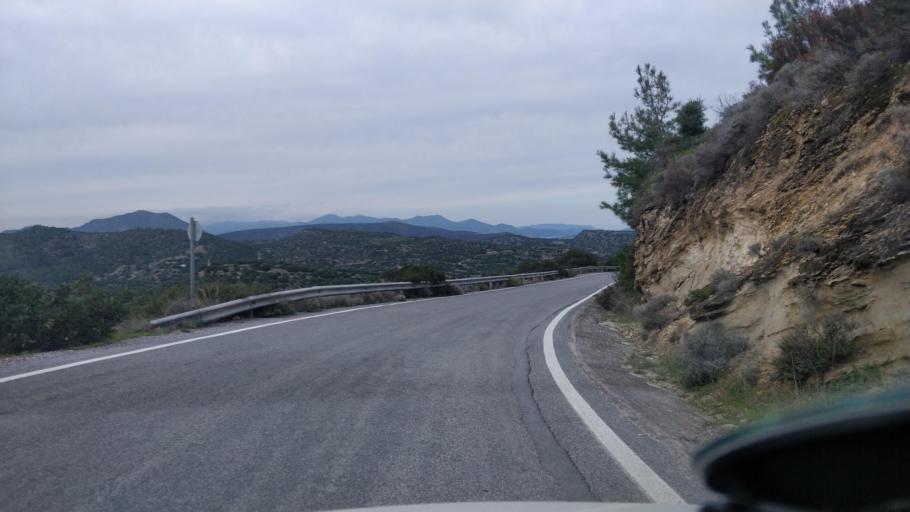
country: GR
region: Crete
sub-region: Nomos Lasithiou
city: Kritsa
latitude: 35.1050
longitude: 25.7114
